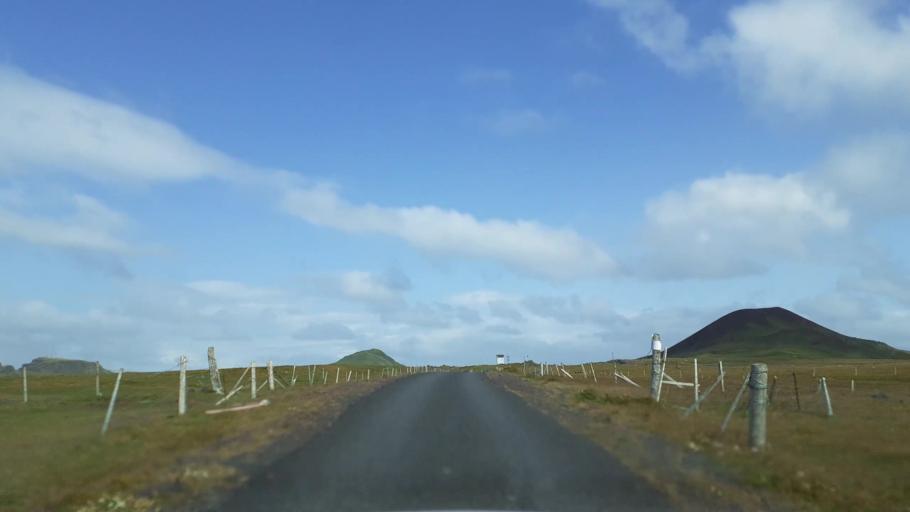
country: IS
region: South
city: Vestmannaeyjar
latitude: 63.4202
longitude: -20.2800
